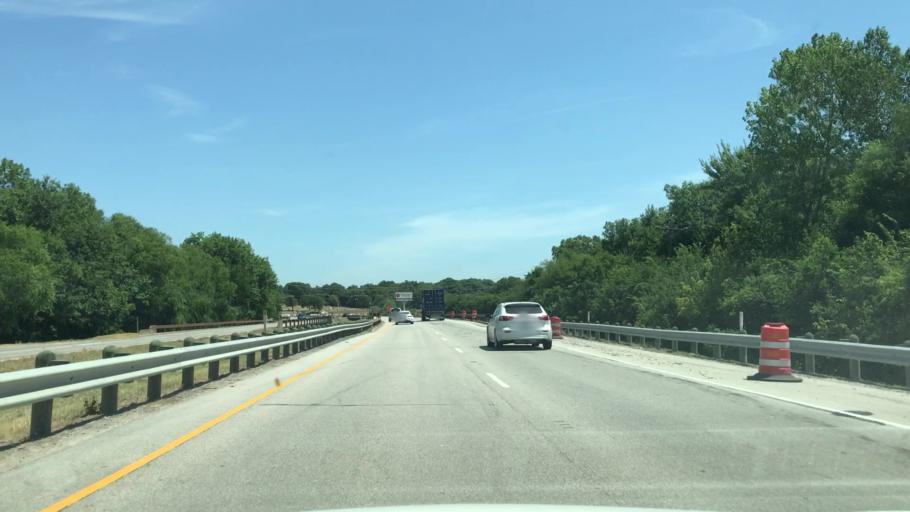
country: US
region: Texas
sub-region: Collin County
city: Fairview
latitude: 33.1722
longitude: -96.6234
